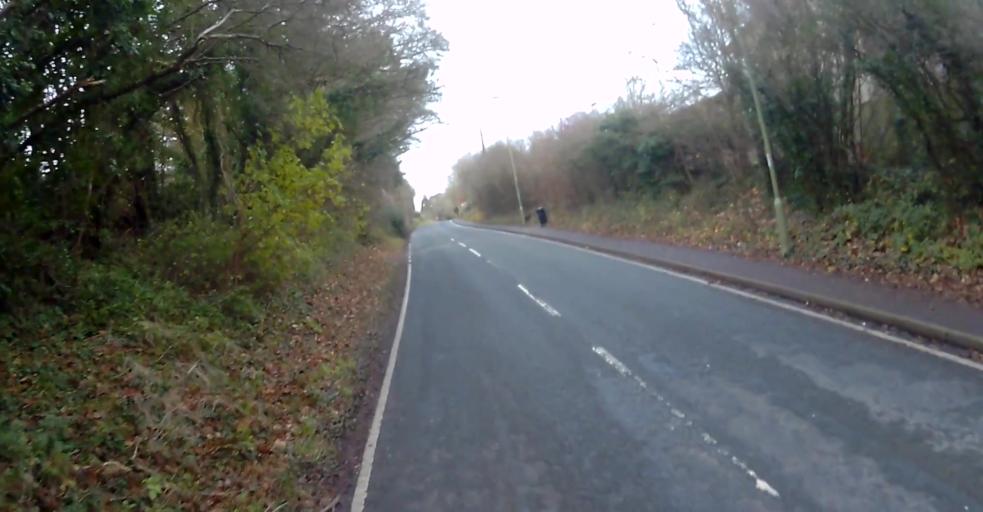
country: GB
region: England
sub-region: Hampshire
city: Overton
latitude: 51.2496
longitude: -1.2638
